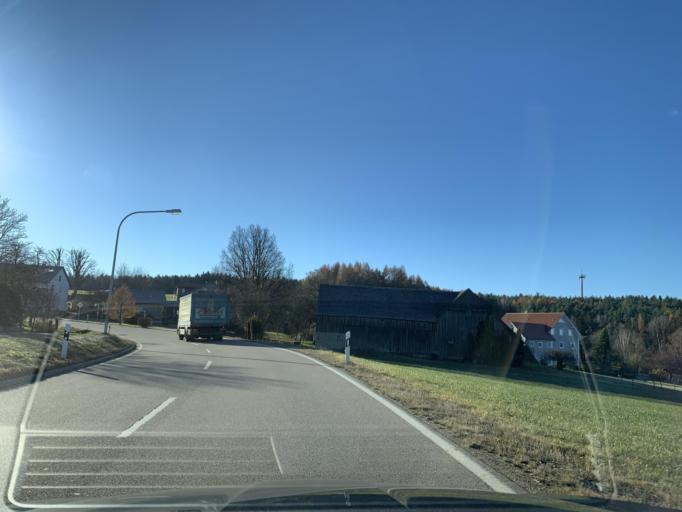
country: DE
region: Bavaria
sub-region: Upper Palatinate
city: Oberviechtach
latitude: 49.4413
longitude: 12.4151
